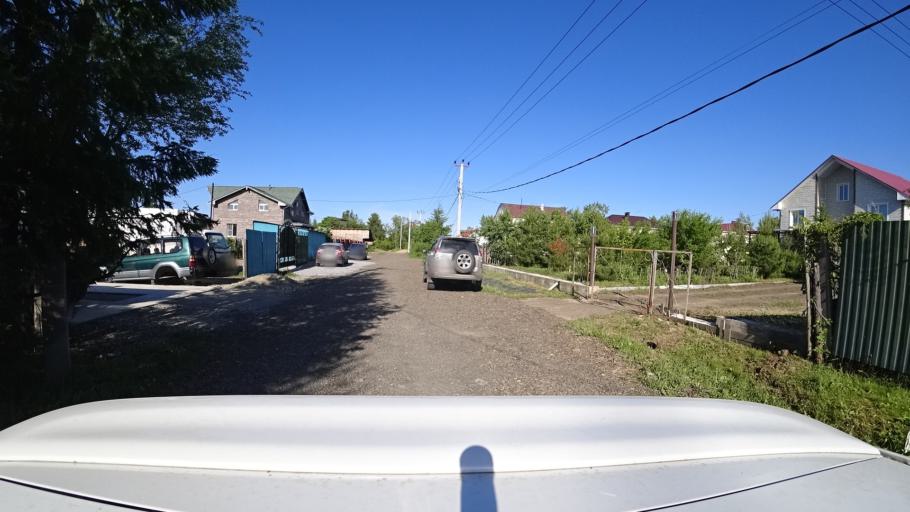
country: RU
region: Khabarovsk Krai
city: Topolevo
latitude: 48.5438
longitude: 135.1750
